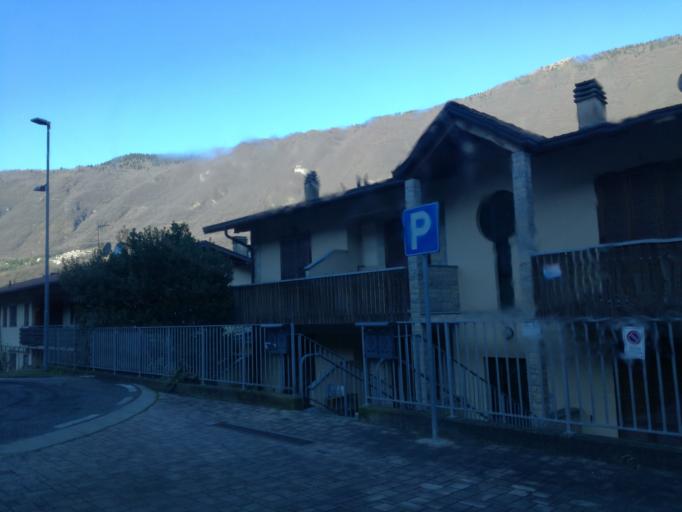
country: IT
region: Lombardy
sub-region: Provincia di Bergamo
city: Endine
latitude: 45.7864
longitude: 9.9628
